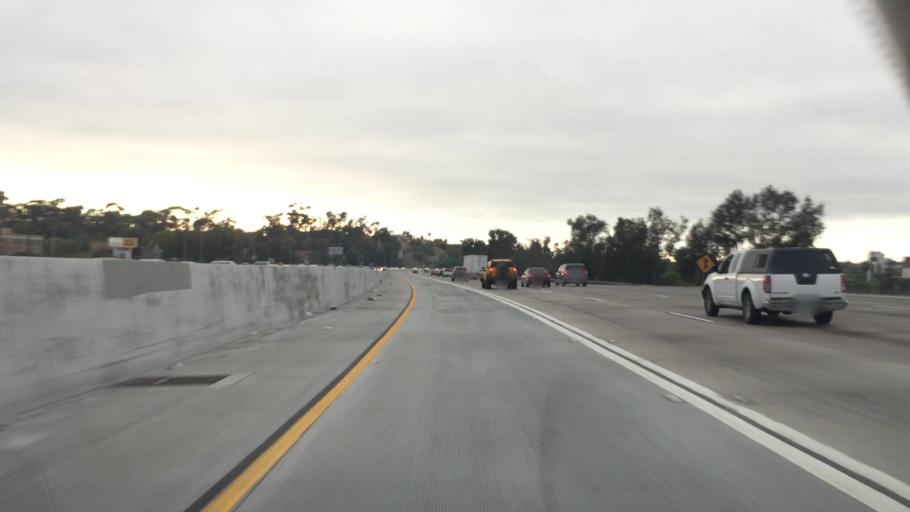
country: US
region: California
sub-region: San Diego County
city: Chula Vista
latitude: 32.6487
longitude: -117.0623
